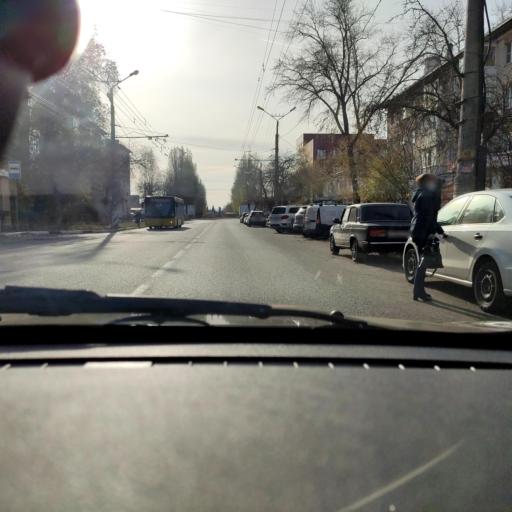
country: RU
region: Samara
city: Tol'yatti
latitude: 53.5127
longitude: 49.4178
